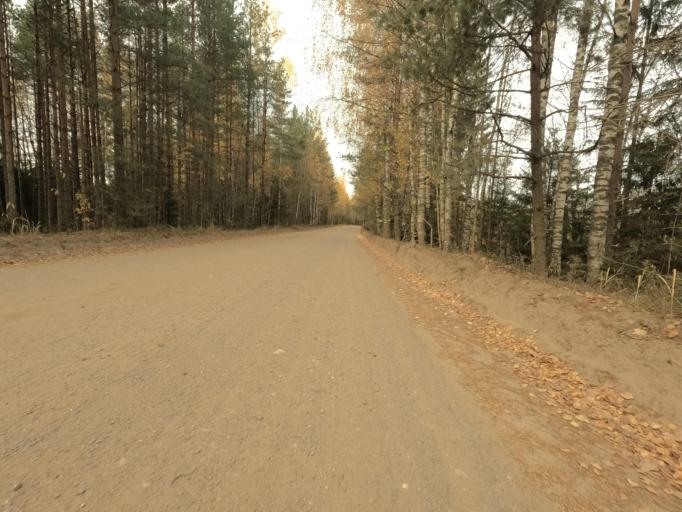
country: RU
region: Leningrad
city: Priladozhskiy
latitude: 59.6835
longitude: 31.3627
